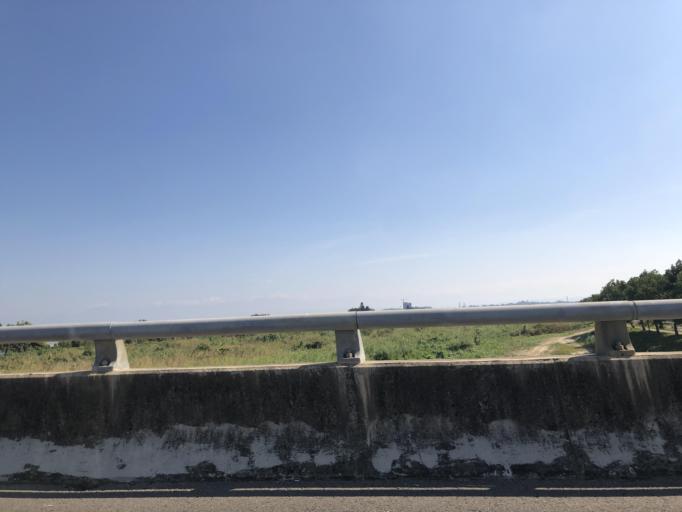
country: TW
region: Taiwan
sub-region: Tainan
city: Tainan
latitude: 23.0164
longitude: 120.2888
